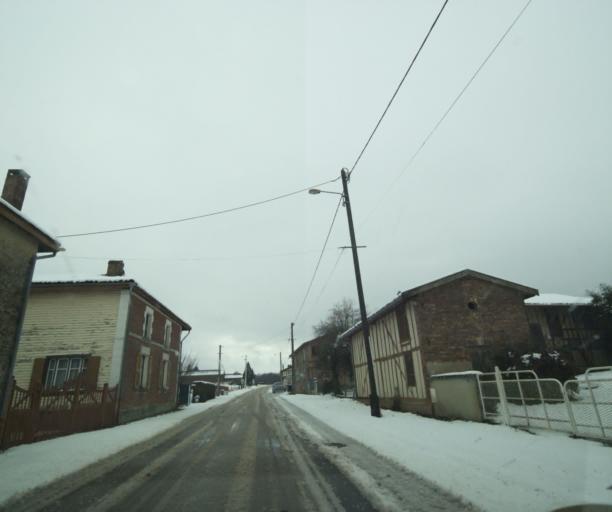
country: FR
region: Champagne-Ardenne
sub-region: Departement de la Haute-Marne
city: Montier-en-Der
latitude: 48.4320
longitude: 4.7277
